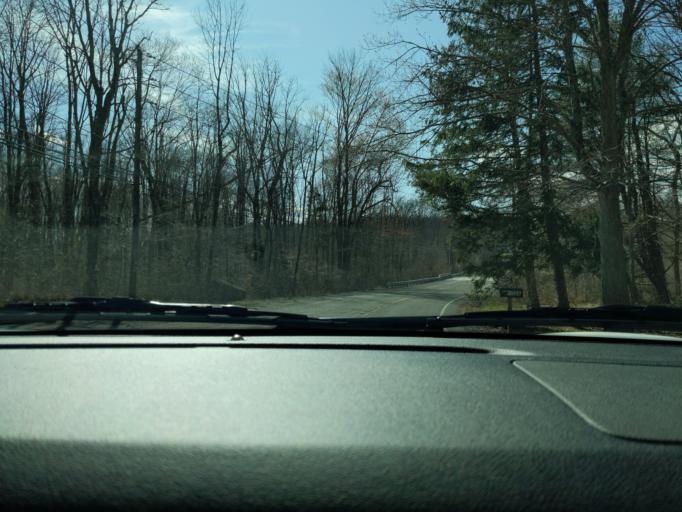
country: US
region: Pennsylvania
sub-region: Bucks County
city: Richlandtown
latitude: 40.4591
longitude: -75.2746
